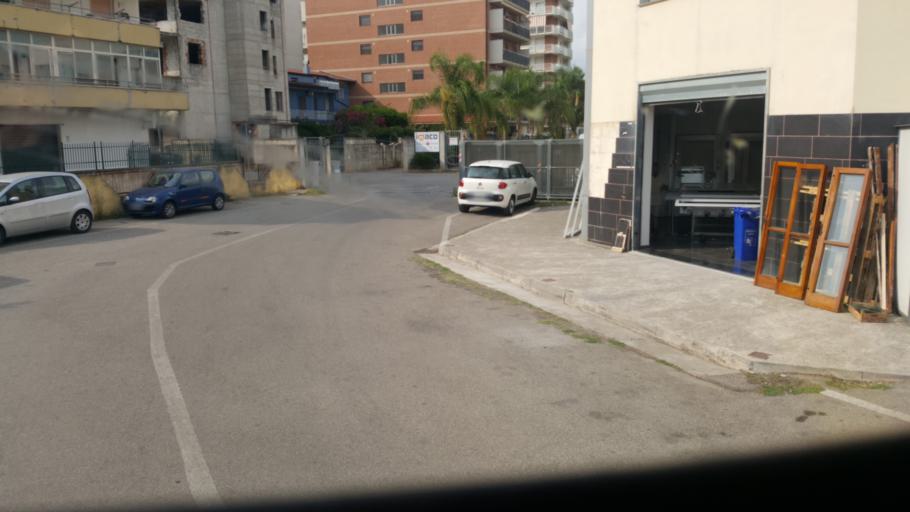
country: IT
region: Campania
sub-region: Provincia di Salerno
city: Battipaglia
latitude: 40.5981
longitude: 14.9846
